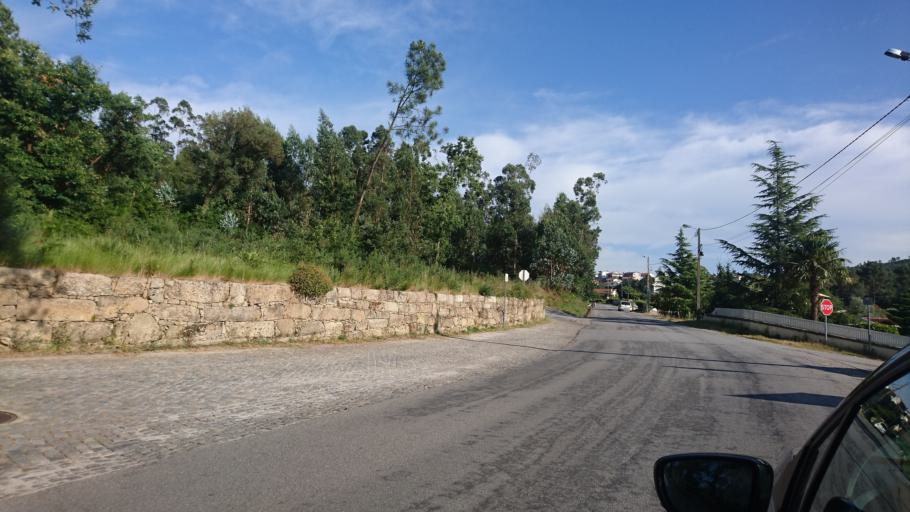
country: PT
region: Porto
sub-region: Paredes
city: Recarei
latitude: 41.1293
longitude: -8.3738
